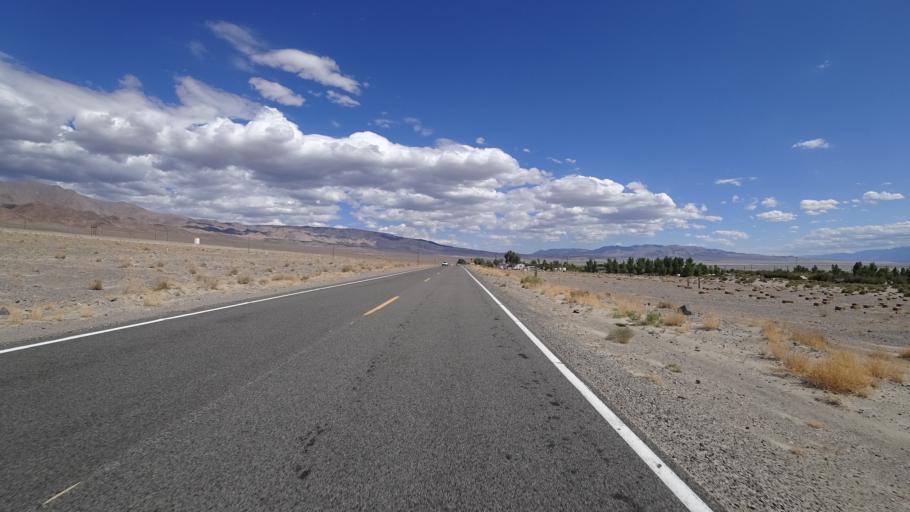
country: US
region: California
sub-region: Inyo County
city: Lone Pine
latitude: 36.4923
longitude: -117.8741
